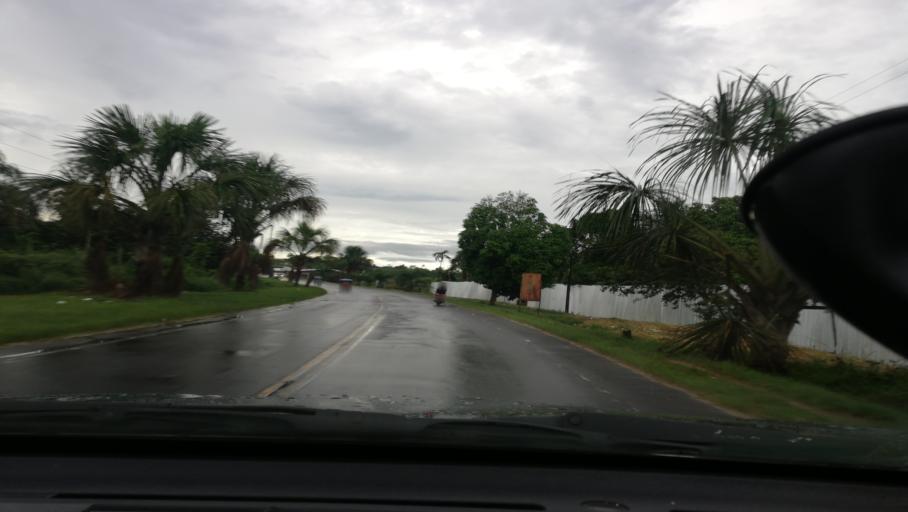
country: PE
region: Loreto
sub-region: Provincia de Maynas
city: Iquitos
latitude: -3.8504
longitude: -73.3385
